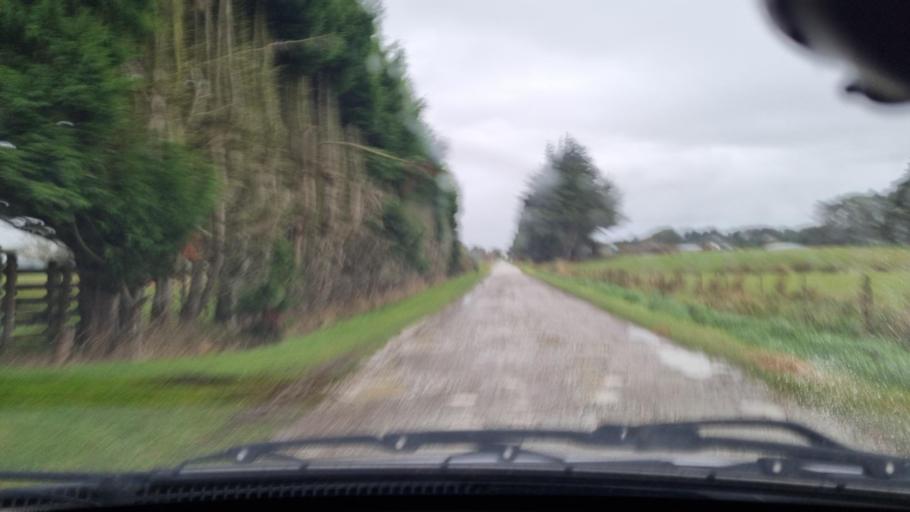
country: NZ
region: Southland
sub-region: Invercargill City
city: Invercargill
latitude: -46.4385
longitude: 168.3896
